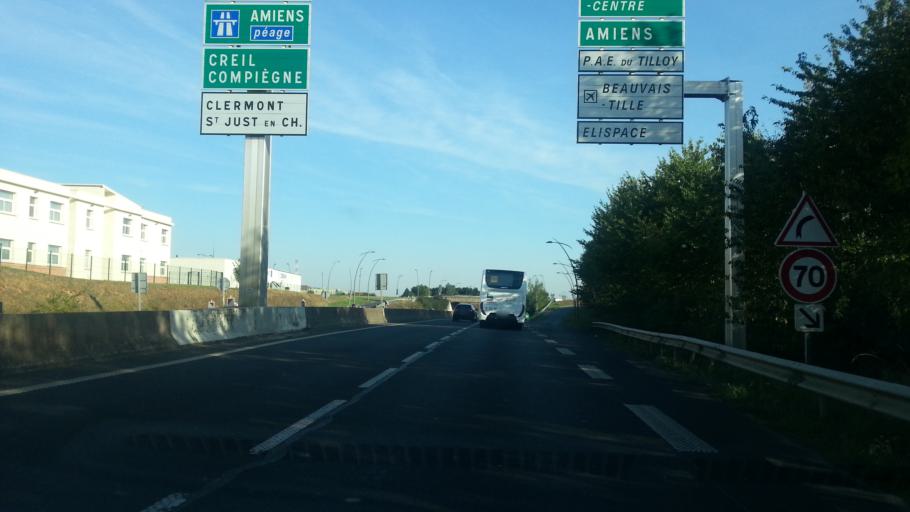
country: FR
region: Picardie
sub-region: Departement de l'Oise
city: Tille
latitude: 49.4540
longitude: 2.0962
